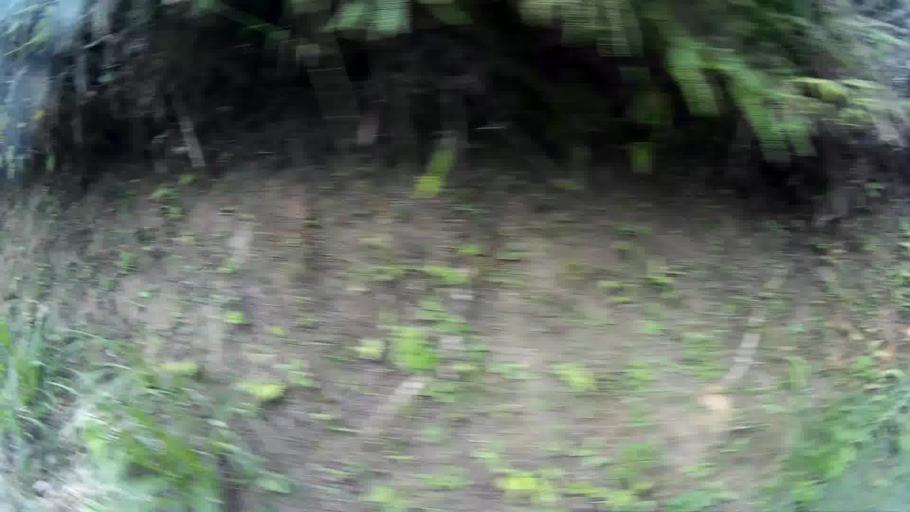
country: CO
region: Valle del Cauca
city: Ulloa
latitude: 4.7287
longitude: -75.7113
